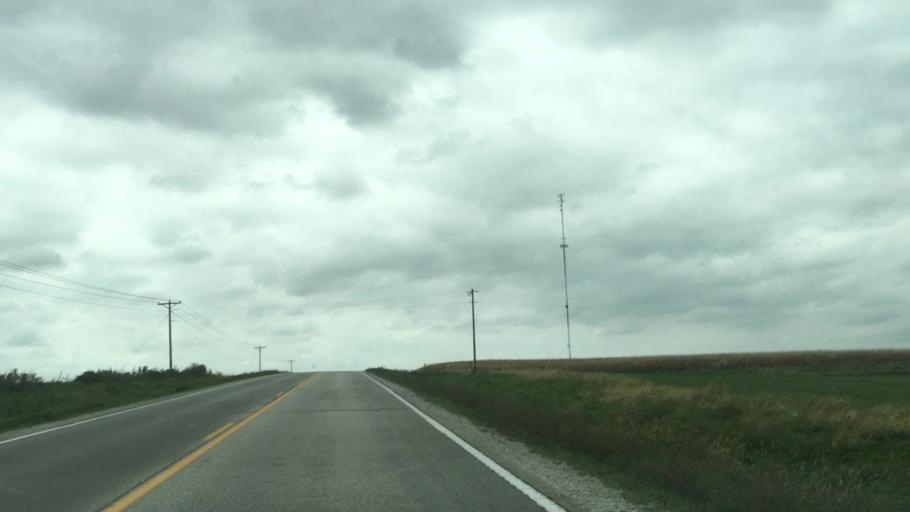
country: US
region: Minnesota
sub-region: Fillmore County
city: Preston
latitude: 43.7318
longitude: -92.0782
